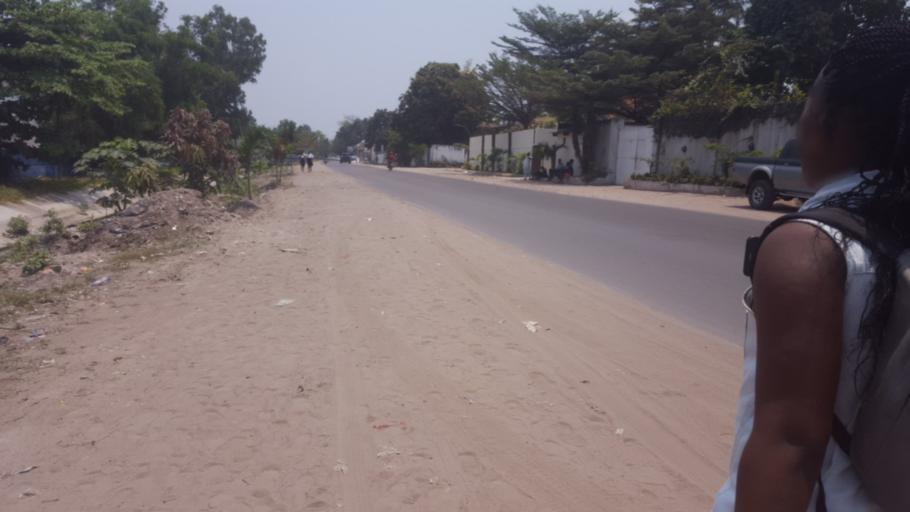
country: CD
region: Kinshasa
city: Kinshasa
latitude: -4.3180
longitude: 15.2888
